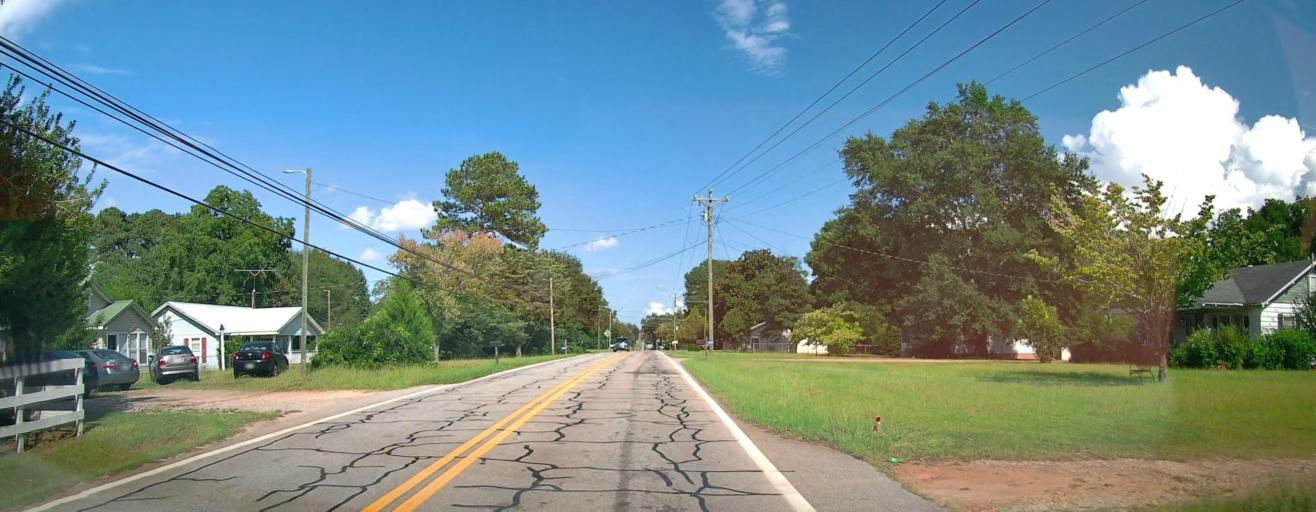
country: US
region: Georgia
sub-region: Upson County
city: Hannahs Mill
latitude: 32.9350
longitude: -84.3511
